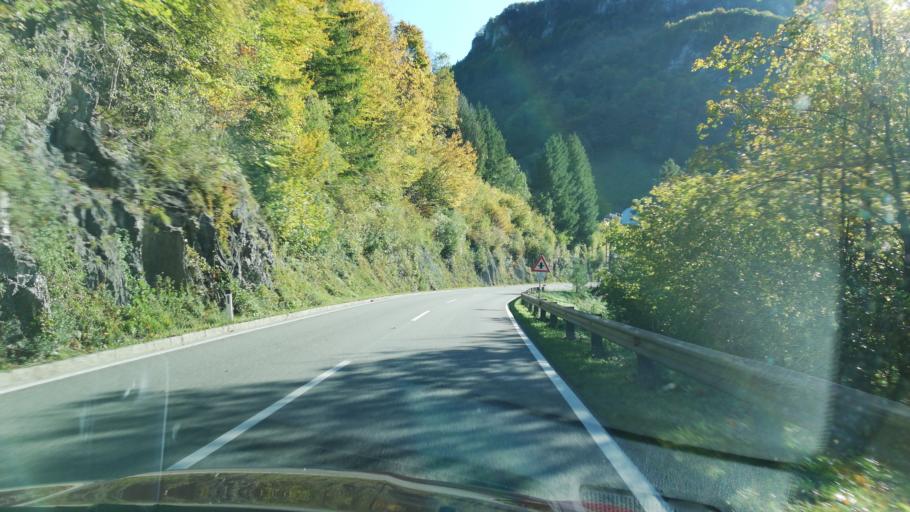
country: AT
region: Upper Austria
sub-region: Politischer Bezirk Steyr-Land
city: Maria Neustift
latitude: 47.8794
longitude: 14.5999
